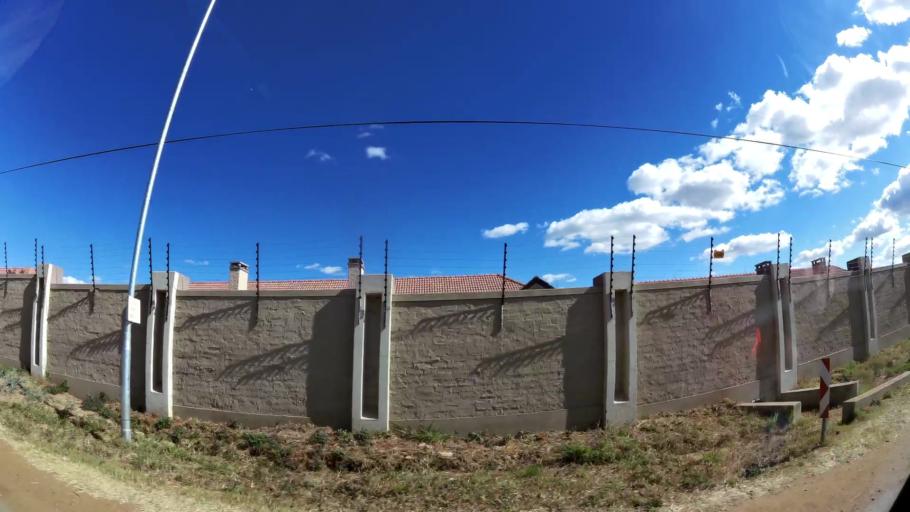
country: ZA
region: Limpopo
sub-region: Capricorn District Municipality
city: Polokwane
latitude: -23.8769
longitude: 29.5142
